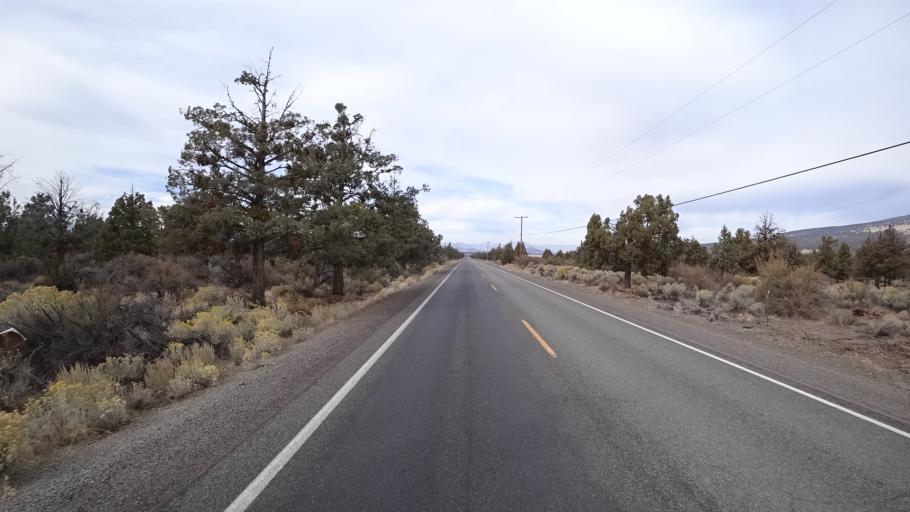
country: US
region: California
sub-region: Siskiyou County
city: Weed
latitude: 41.5818
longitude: -122.2912
